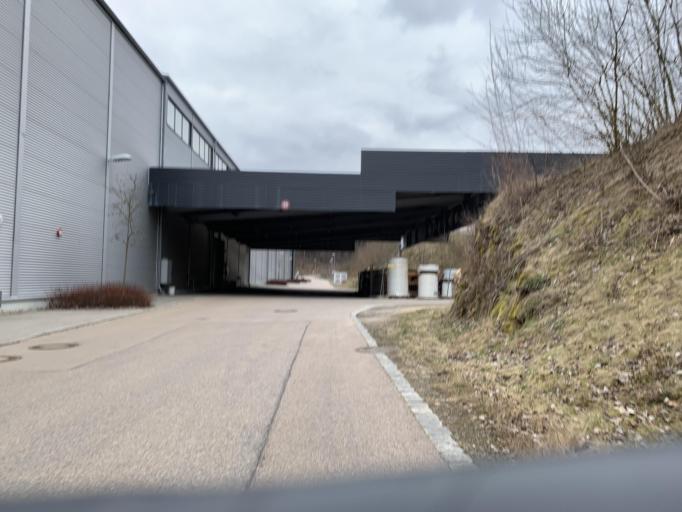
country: DE
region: Bavaria
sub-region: Upper Palatinate
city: Neunburg vorm Wald
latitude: 49.3408
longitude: 12.3978
